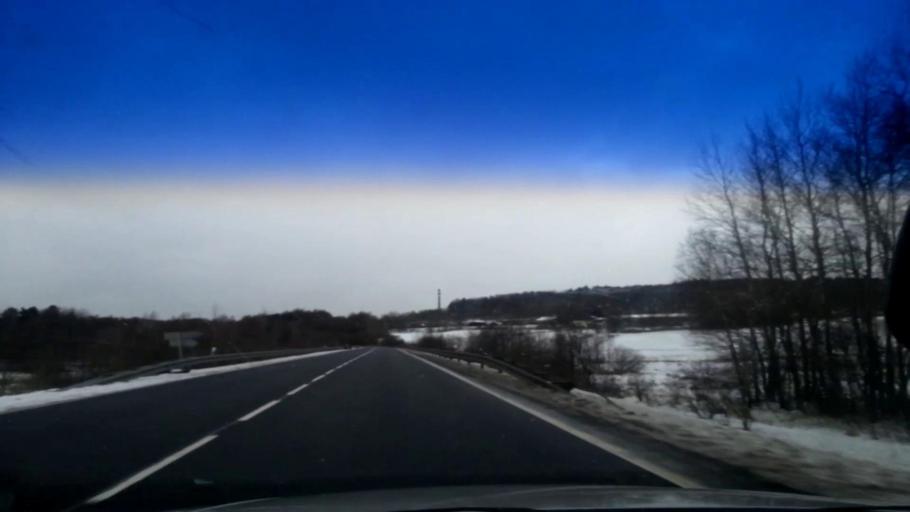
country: CZ
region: Karlovarsky
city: As
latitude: 50.2040
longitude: 12.1950
